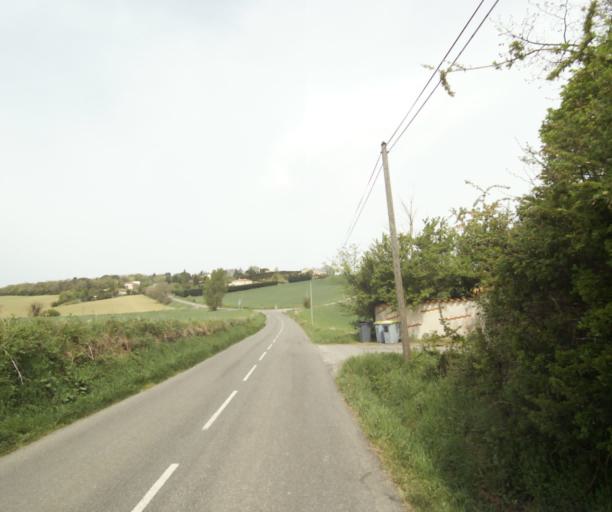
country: FR
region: Midi-Pyrenees
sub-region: Departement de la Haute-Garonne
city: Castanet-Tolosan
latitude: 43.4997
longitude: 1.4853
